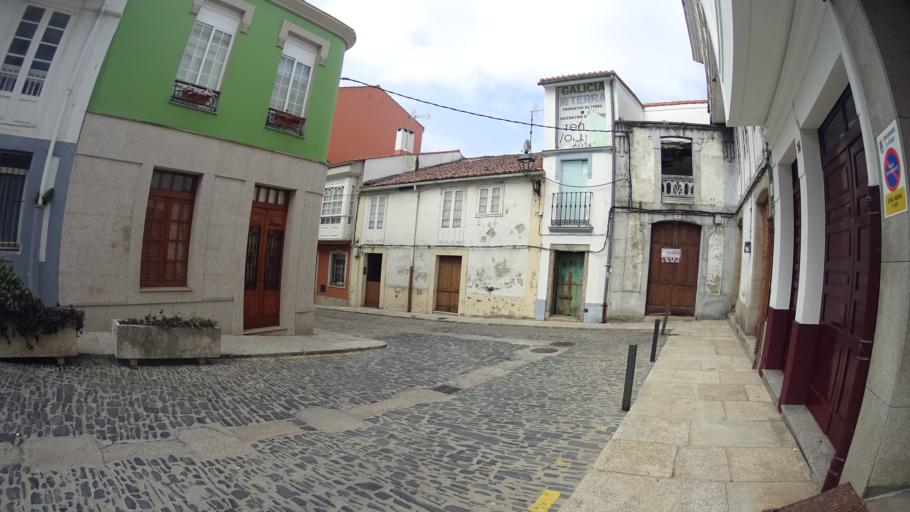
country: ES
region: Galicia
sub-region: Provincia da Coruna
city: Betanzos
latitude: 43.2825
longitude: -8.2124
